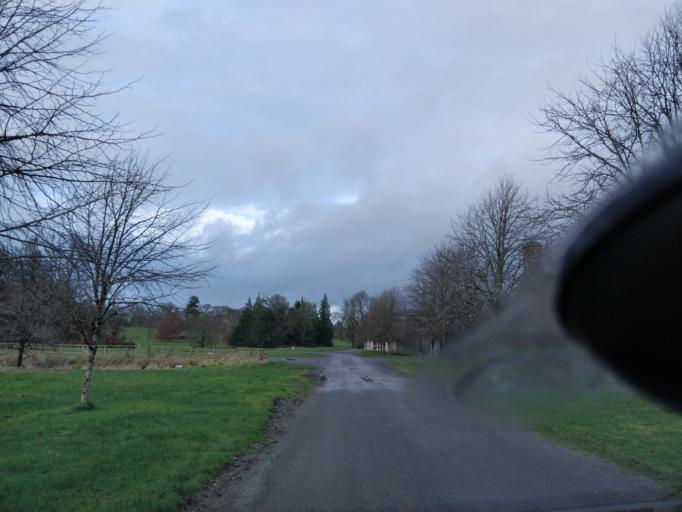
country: IE
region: Leinster
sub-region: An Longfort
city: Lanesborough
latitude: 53.7756
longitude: -8.0983
